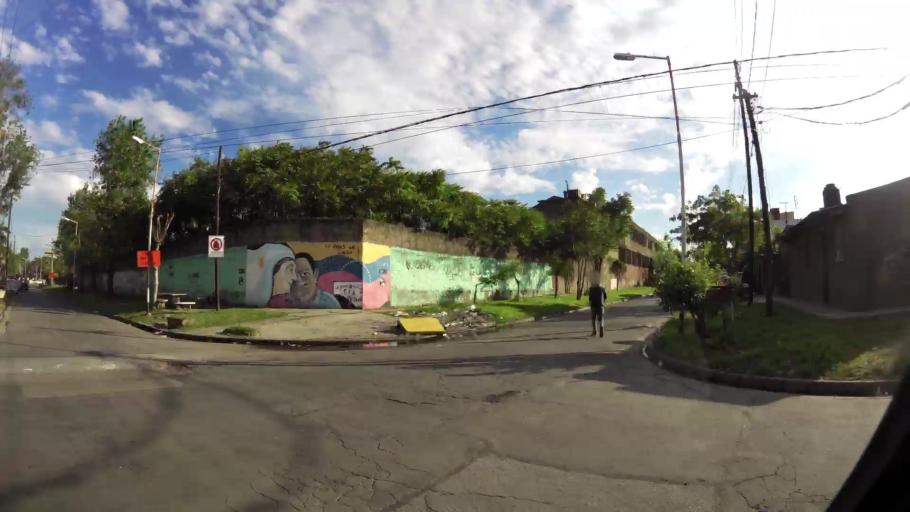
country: AR
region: Buenos Aires
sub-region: Partido de Lanus
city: Lanus
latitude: -34.7097
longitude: -58.3505
